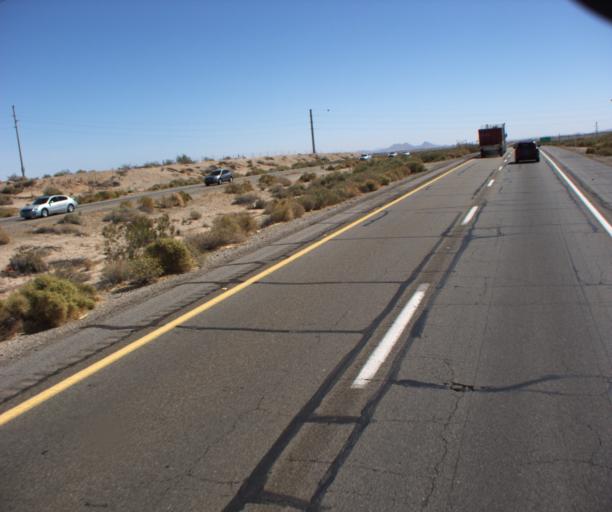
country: US
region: Arizona
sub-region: Yuma County
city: Wellton
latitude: 32.6618
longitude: -114.2629
